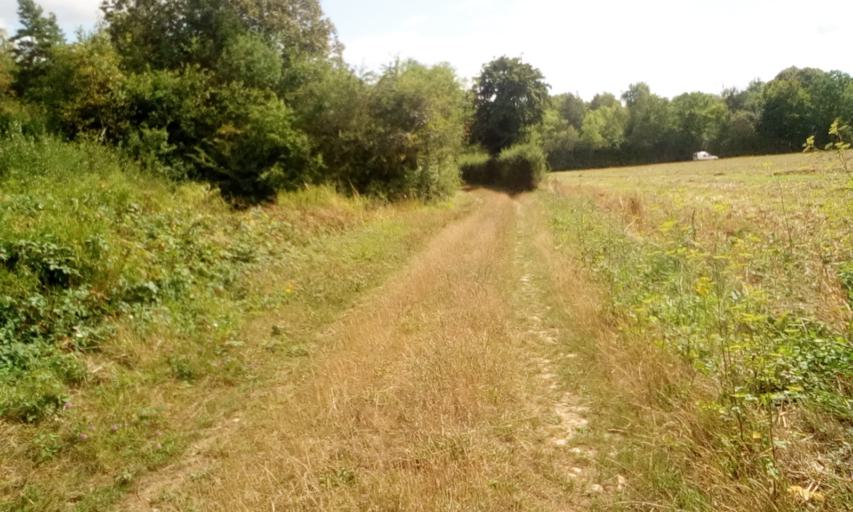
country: FR
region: Lower Normandy
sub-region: Departement du Calvados
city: Cagny
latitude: 49.1094
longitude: -0.2494
